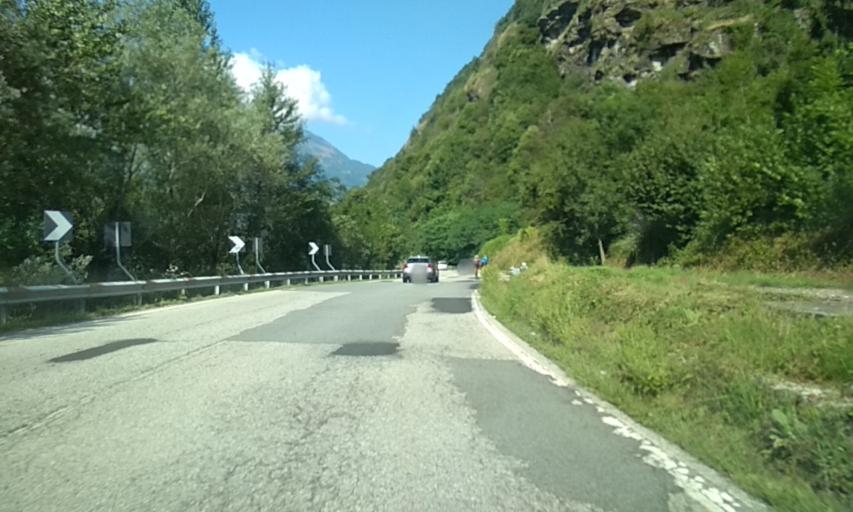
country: IT
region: Piedmont
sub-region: Provincia di Torino
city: Ribordone
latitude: 45.4069
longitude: 7.5013
